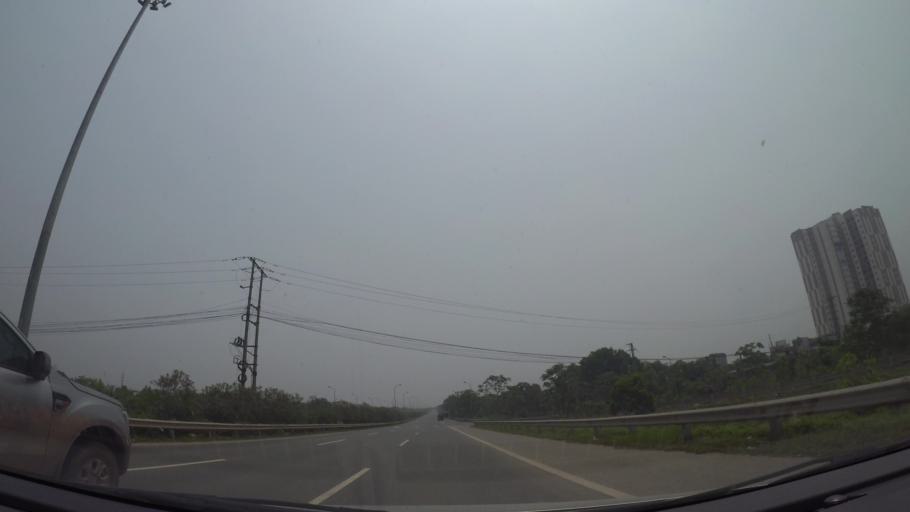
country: VN
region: Ha Noi
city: Lien Quan
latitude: 20.9898
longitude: 105.5288
